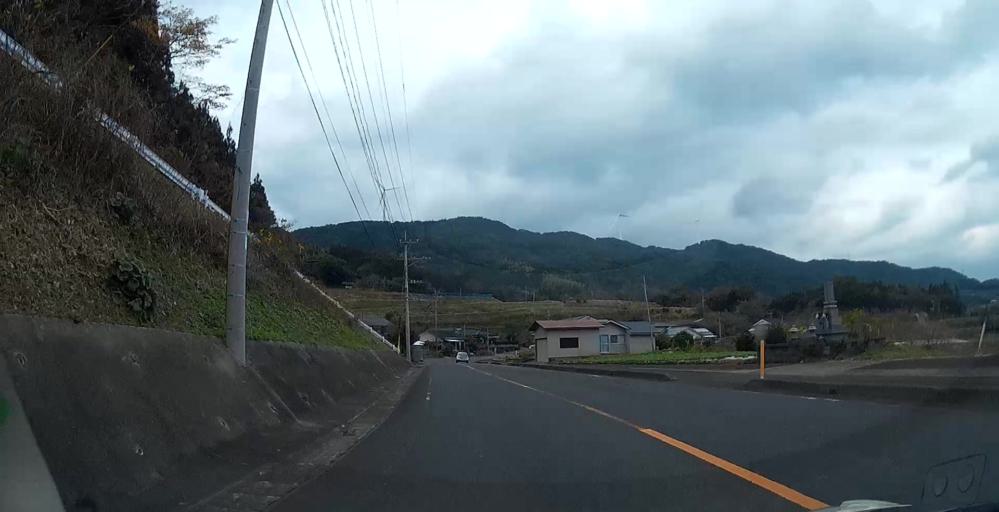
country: JP
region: Kagoshima
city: Akune
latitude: 32.1010
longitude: 130.1674
